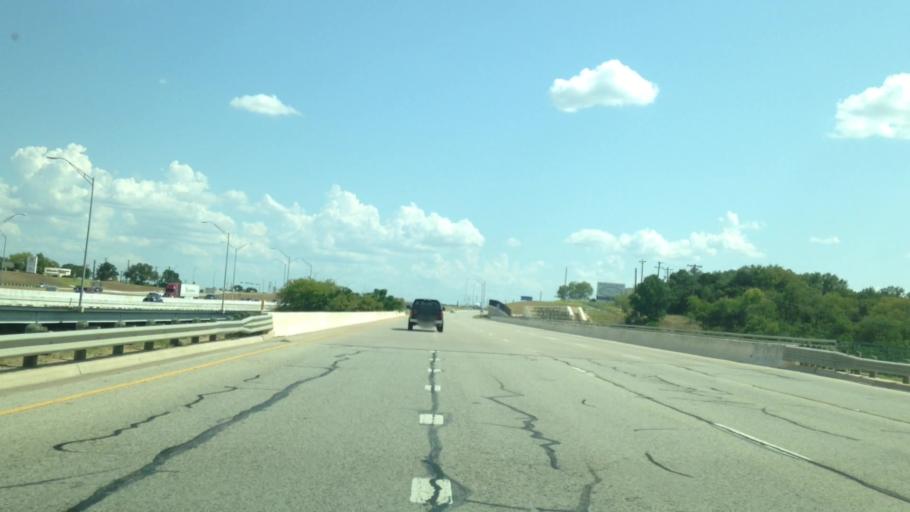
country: US
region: Texas
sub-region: Williamson County
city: Georgetown
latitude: 30.6270
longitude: -97.6920
